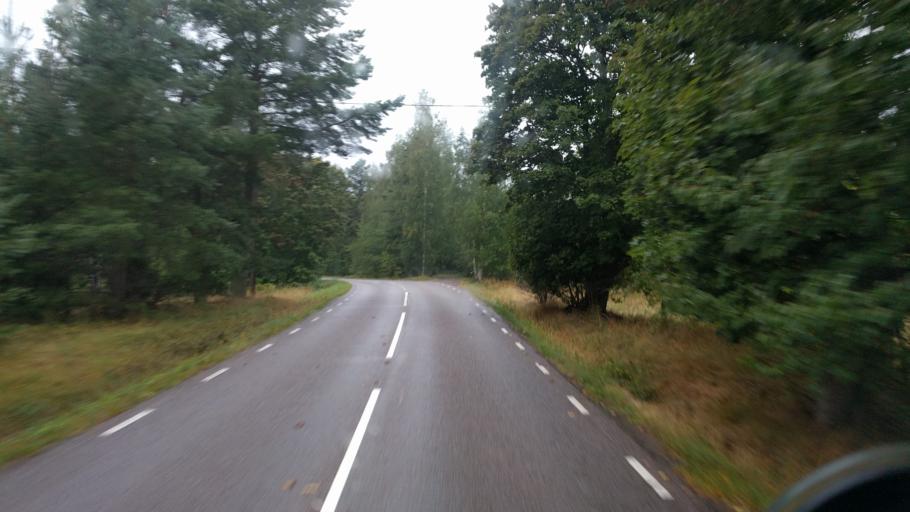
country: SE
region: Kalmar
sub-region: Vasterviks Kommun
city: Gamleby
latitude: 57.8187
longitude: 16.4668
